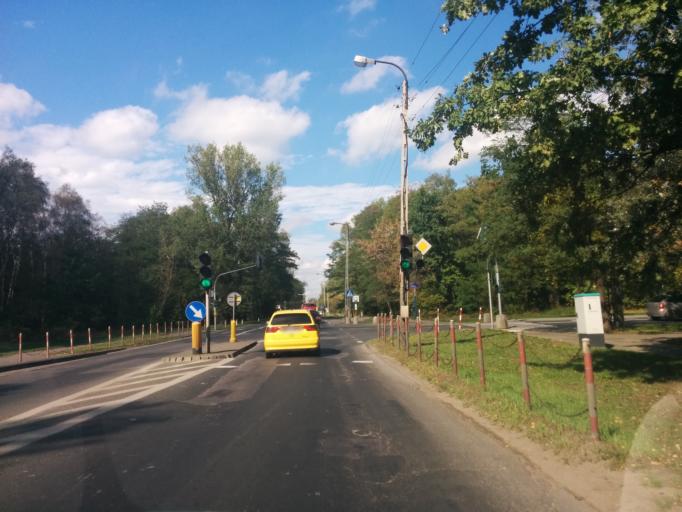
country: PL
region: Masovian Voivodeship
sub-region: Warszawa
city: Targowek
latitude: 52.3031
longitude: 21.0098
